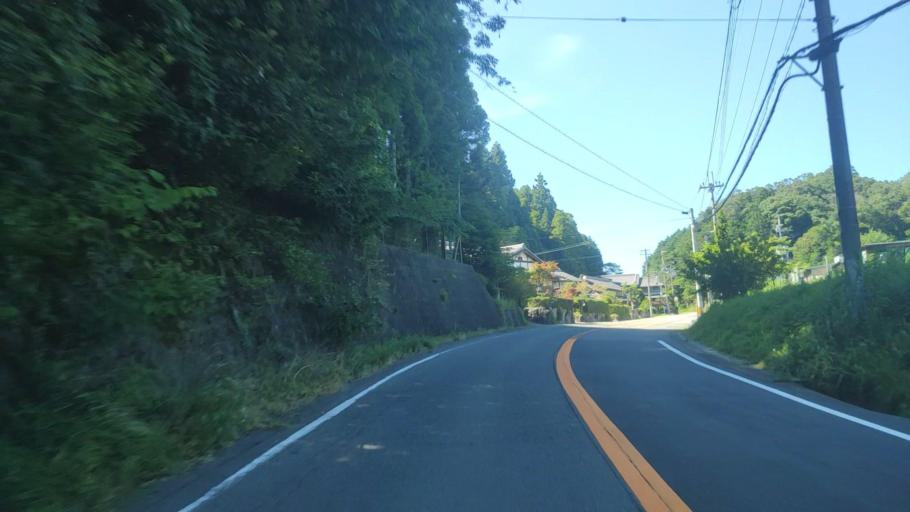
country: JP
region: Nara
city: Haibara-akanedai
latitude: 34.4571
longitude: 135.9347
